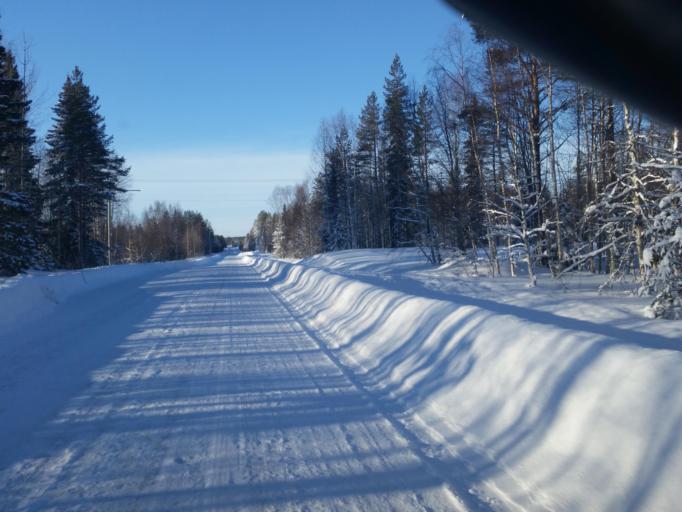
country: SE
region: Norrbotten
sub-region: Pitea Kommun
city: Roknas
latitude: 65.1979
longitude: 21.1269
